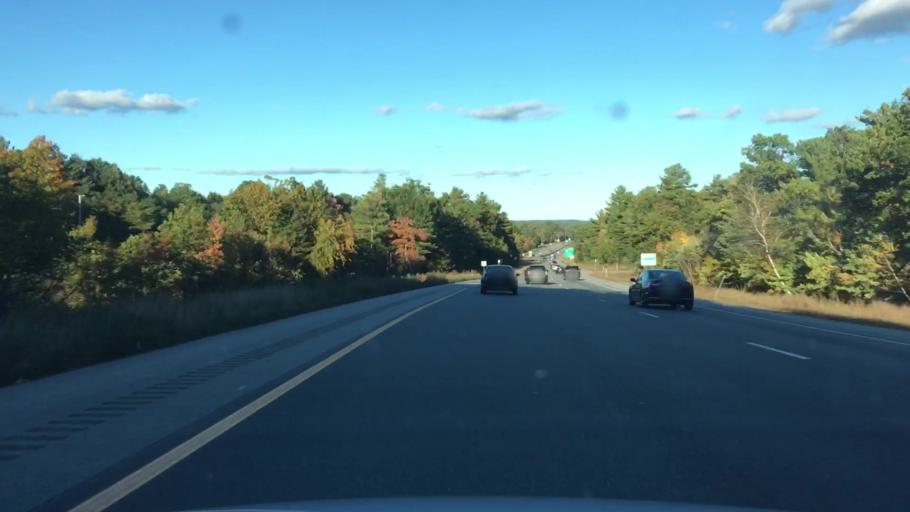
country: US
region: New Hampshire
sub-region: Merrimack County
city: South Hooksett
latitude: 43.0016
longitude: -71.4070
